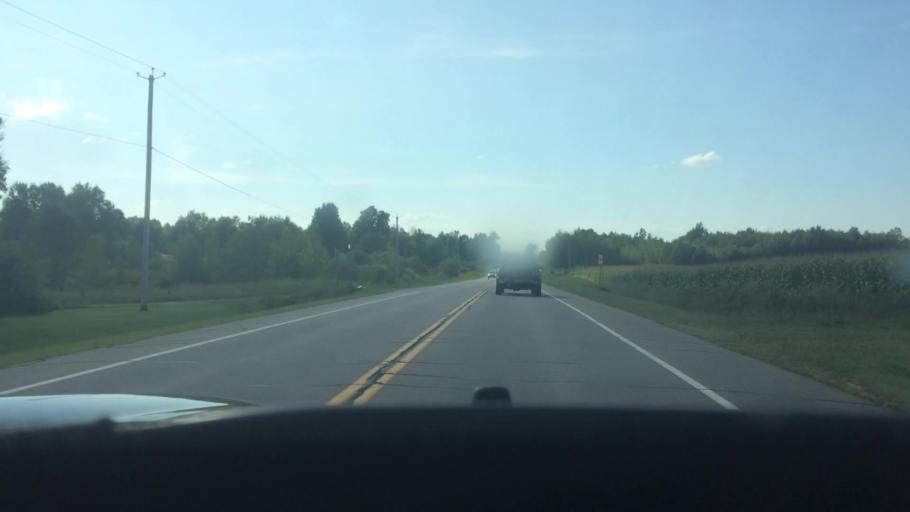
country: US
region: New York
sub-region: Franklin County
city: Malone
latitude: 44.8516
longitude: -74.2074
